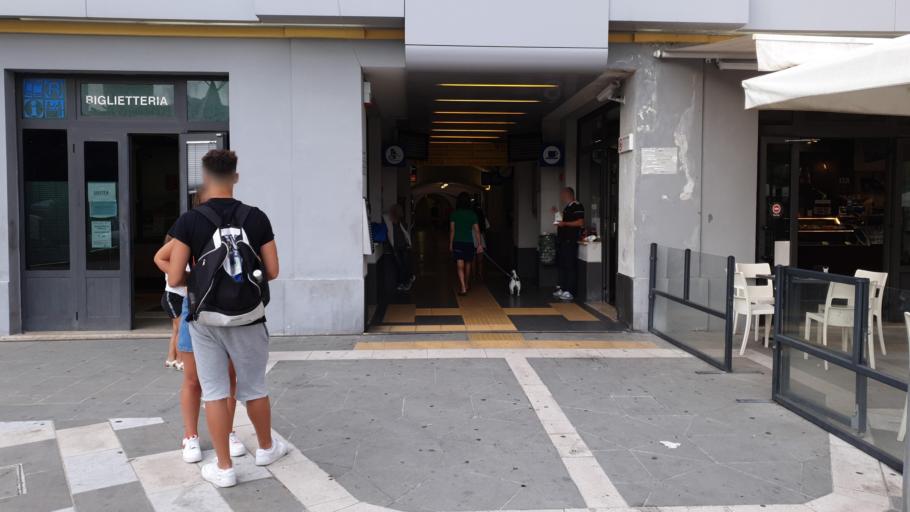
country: IT
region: Liguria
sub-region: Provincia di Genova
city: Rapallo
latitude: 44.3510
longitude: 9.2312
